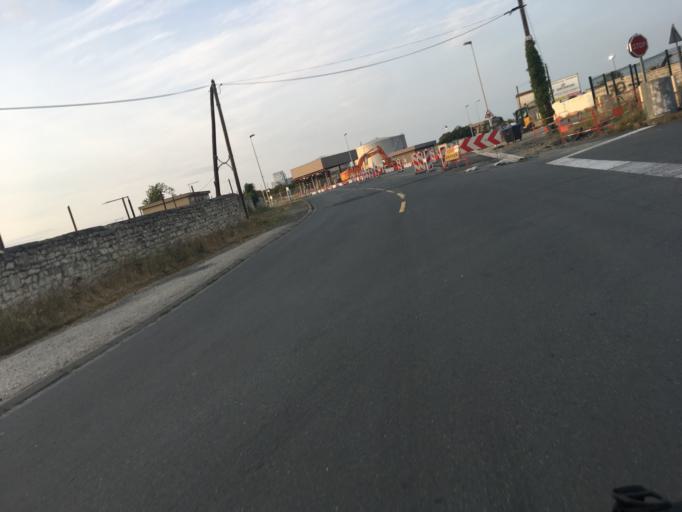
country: FR
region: Poitou-Charentes
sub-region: Departement de la Charente-Maritime
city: Rivedoux-Plage
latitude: 46.1672
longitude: -1.2132
